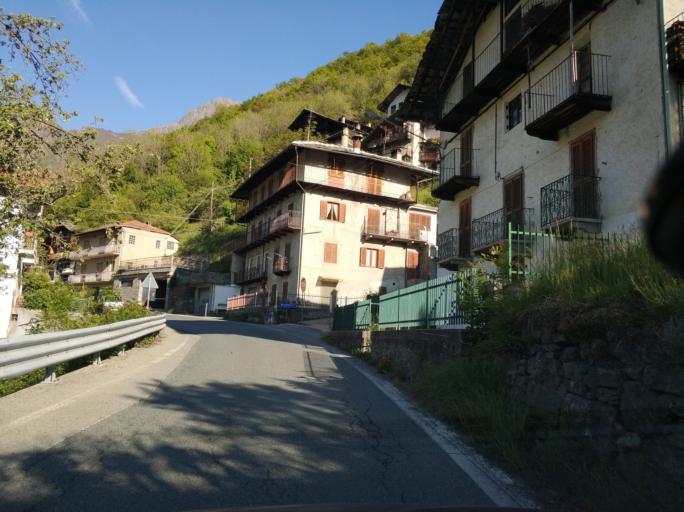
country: IT
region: Piedmont
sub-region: Provincia di Torino
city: Cantoira
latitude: 45.3222
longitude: 7.3540
